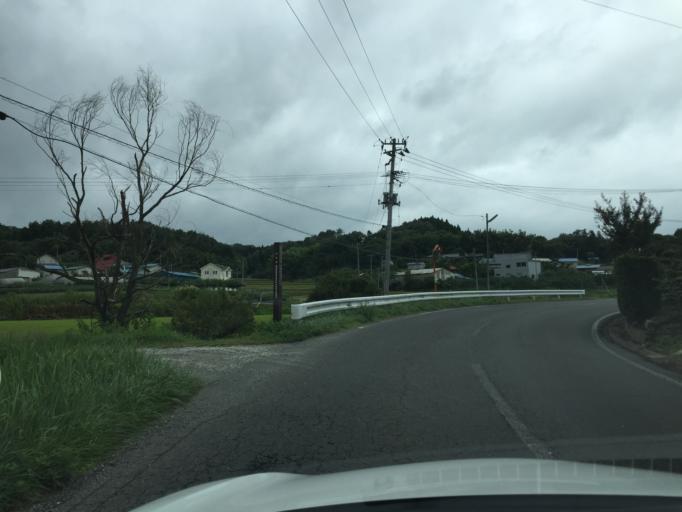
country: JP
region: Fukushima
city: Funehikimachi-funehiki
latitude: 37.4619
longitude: 140.5549
